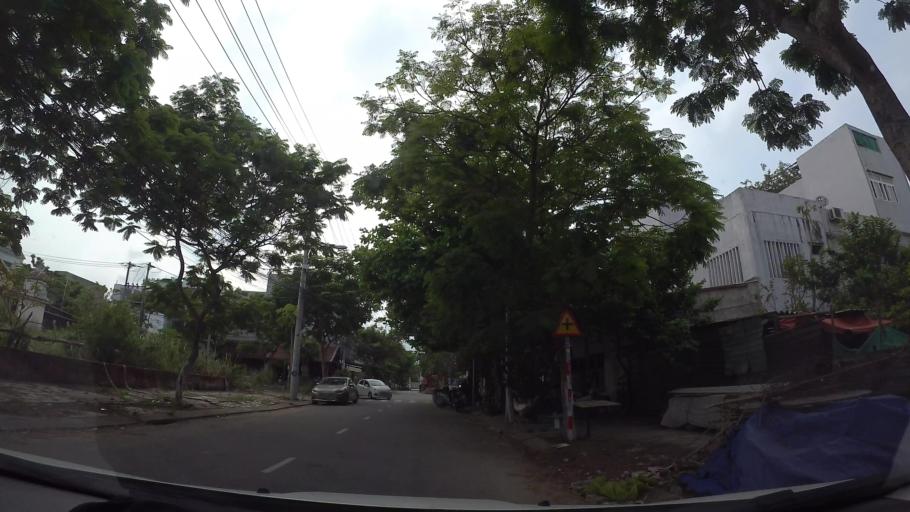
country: VN
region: Da Nang
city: Son Tra
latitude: 16.0755
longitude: 108.2413
